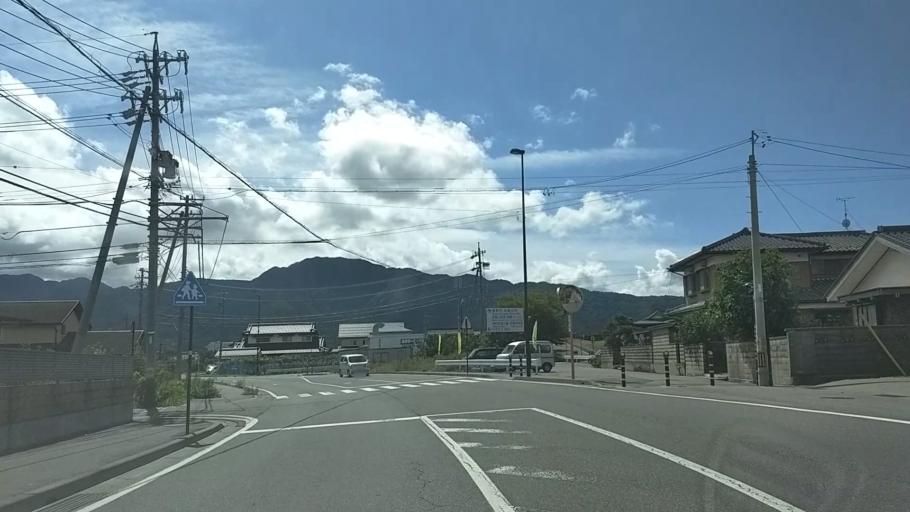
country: JP
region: Nagano
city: Suzaka
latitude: 36.6144
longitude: 138.2503
